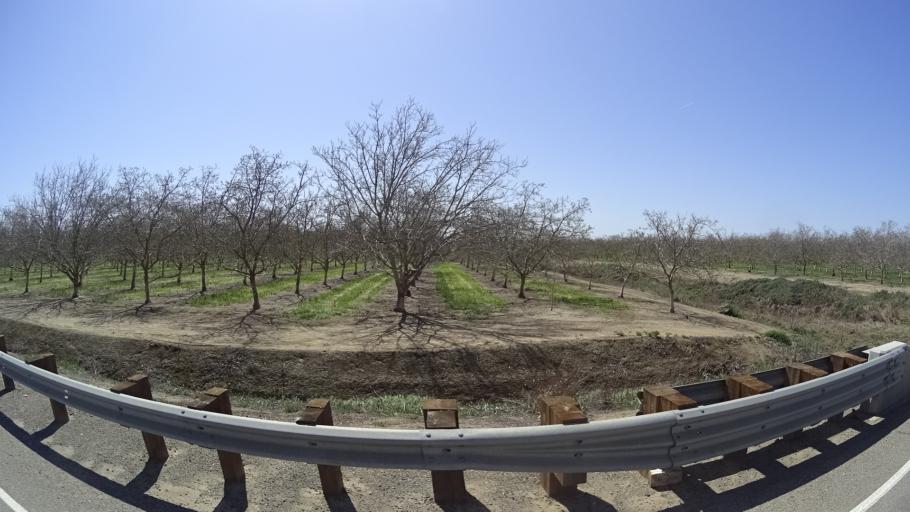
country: US
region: California
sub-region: Butte County
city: Durham
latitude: 39.4642
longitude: -121.9419
